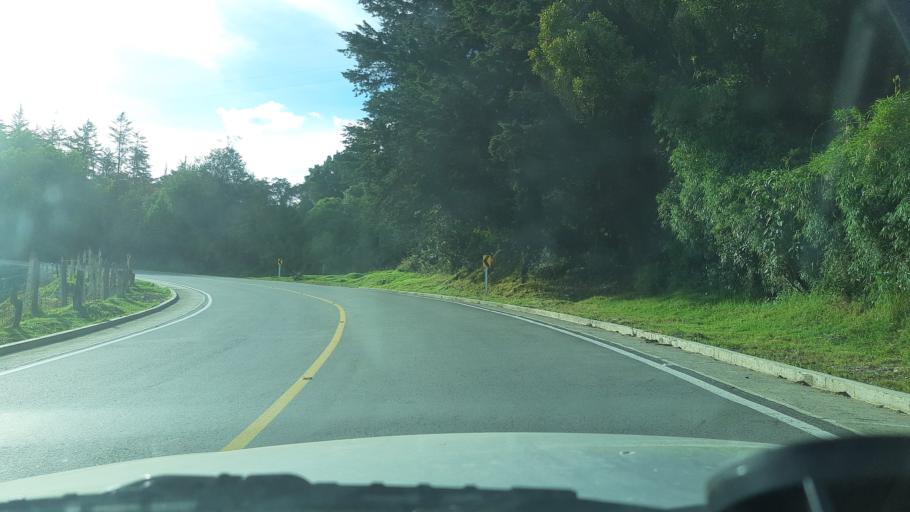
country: CO
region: Cundinamarca
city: Choconta
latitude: 5.0993
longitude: -73.6596
